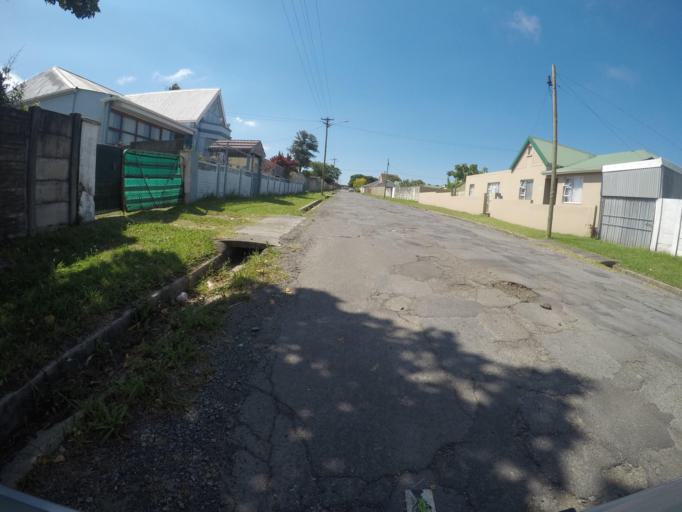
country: ZA
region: Eastern Cape
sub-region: Buffalo City Metropolitan Municipality
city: East London
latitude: -32.9782
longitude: 27.8929
